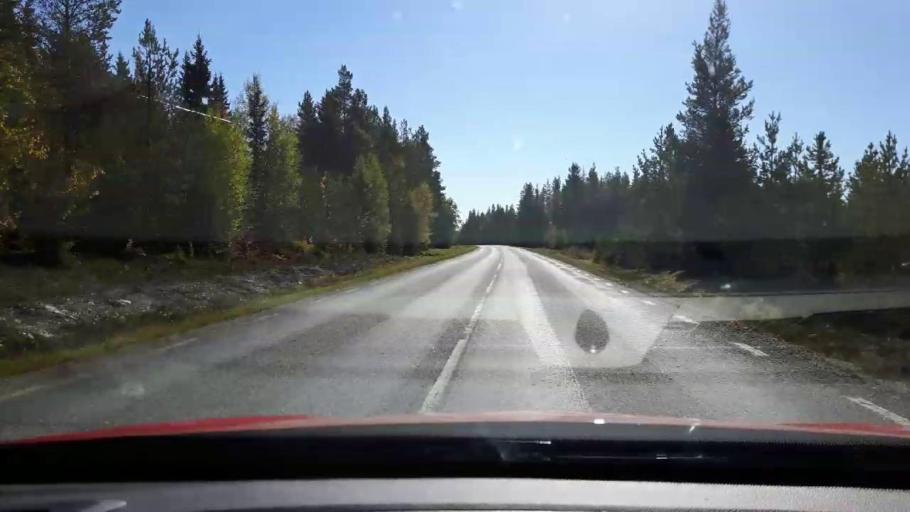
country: SE
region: Jaemtland
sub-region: Harjedalens Kommun
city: Sveg
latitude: 62.4340
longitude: 13.8825
